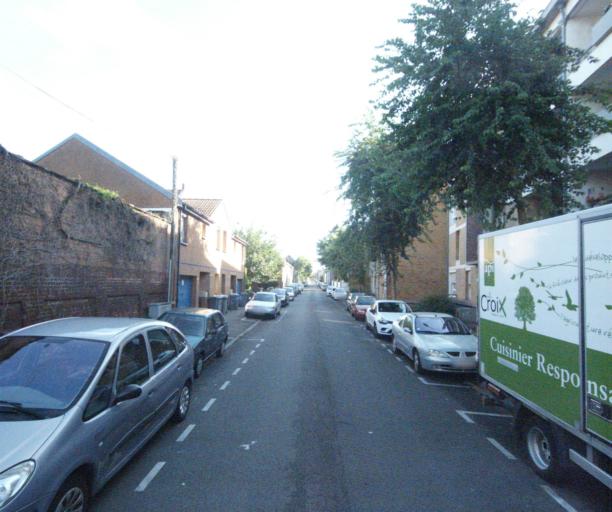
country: FR
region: Nord-Pas-de-Calais
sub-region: Departement du Nord
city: Croix
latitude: 50.6764
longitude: 3.1431
